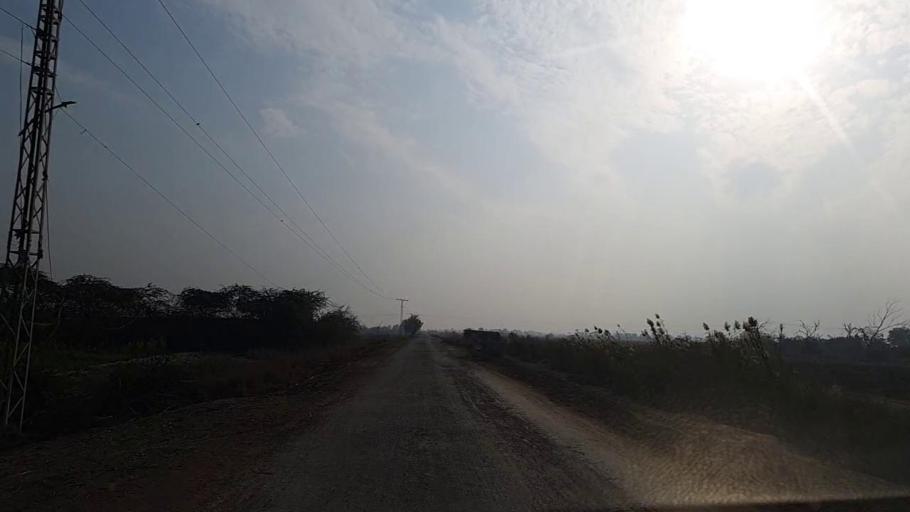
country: PK
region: Sindh
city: Jam Sahib
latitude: 26.3152
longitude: 68.5258
